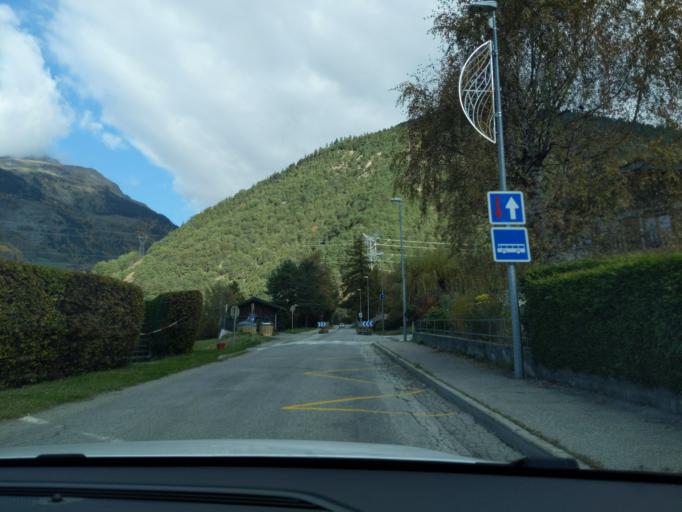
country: FR
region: Rhone-Alpes
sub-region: Departement de la Savoie
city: Seez
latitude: 45.6231
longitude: 6.7948
